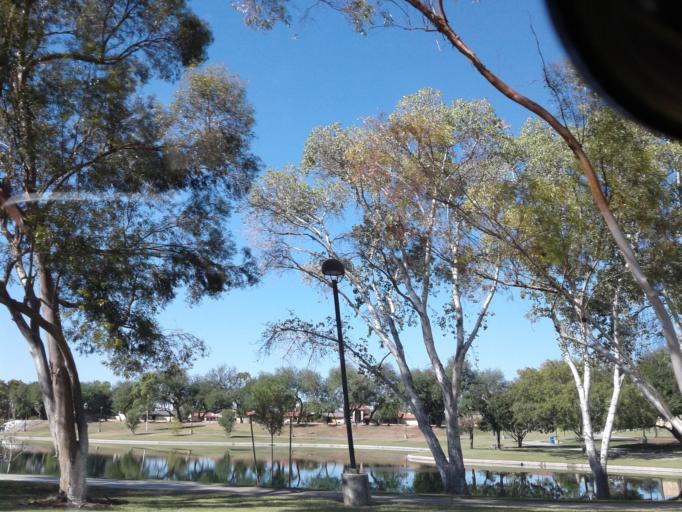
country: US
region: Arizona
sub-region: Maricopa County
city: Scottsdale
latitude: 33.4966
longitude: -111.9093
